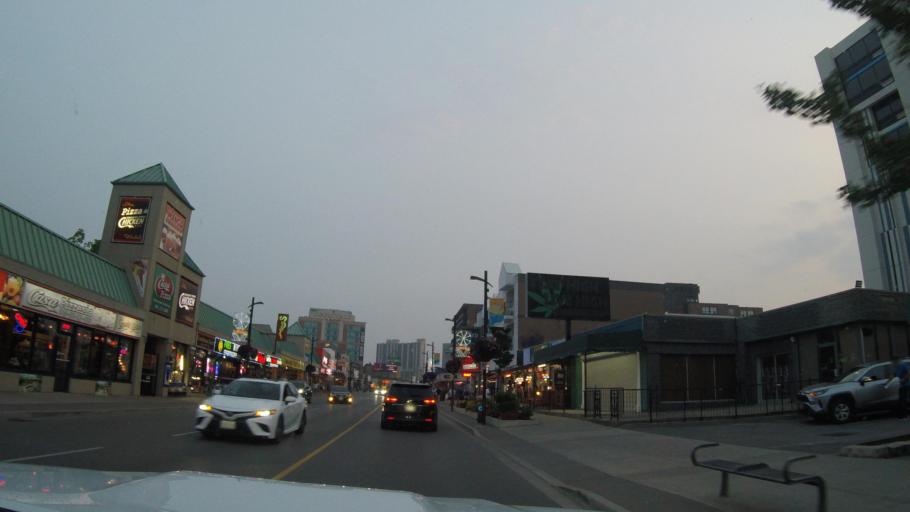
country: CA
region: Ontario
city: Niagara Falls
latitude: 43.0908
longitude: -79.0781
